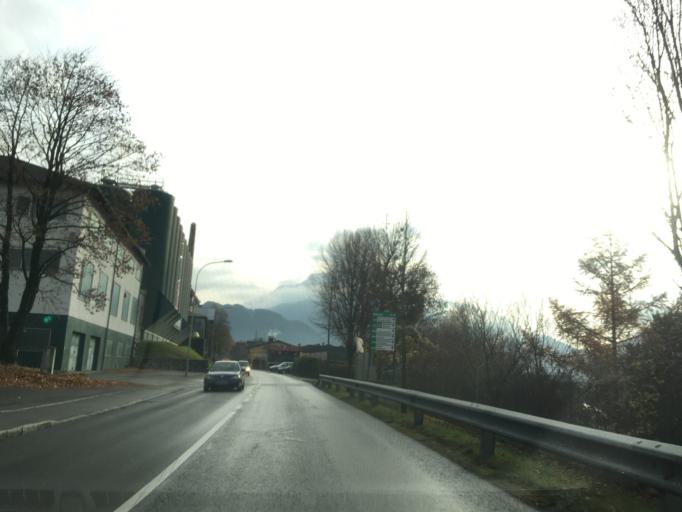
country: AT
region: Vorarlberg
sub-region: Politischer Bezirk Bludenz
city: Bludenz
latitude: 47.1582
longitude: 9.8115
